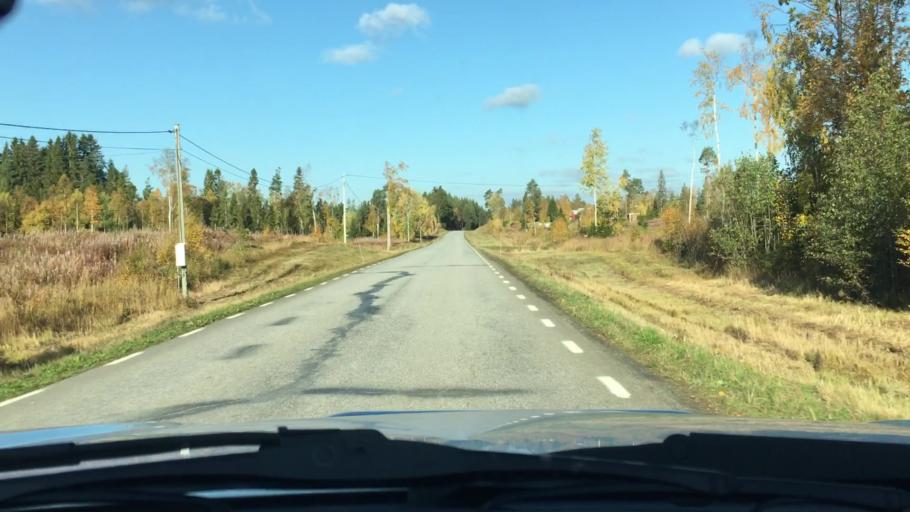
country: SE
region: Jaemtland
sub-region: Krokoms Kommun
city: Krokom
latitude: 63.3047
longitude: 14.2073
